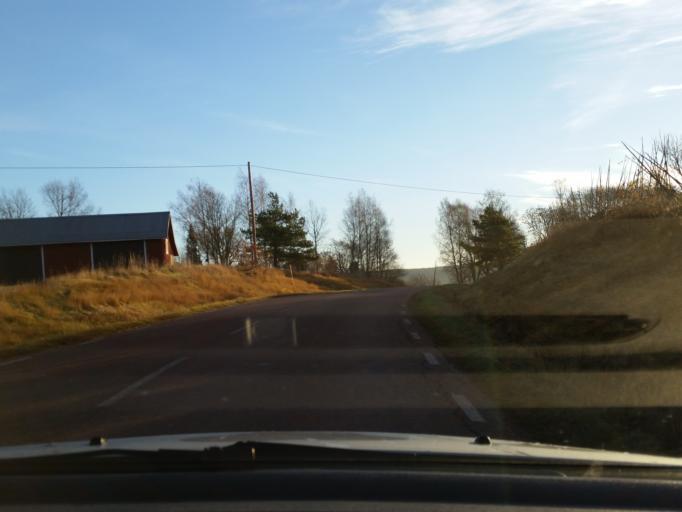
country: AX
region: Alands landsbygd
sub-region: Saltvik
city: Saltvik
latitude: 60.2782
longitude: 20.0727
